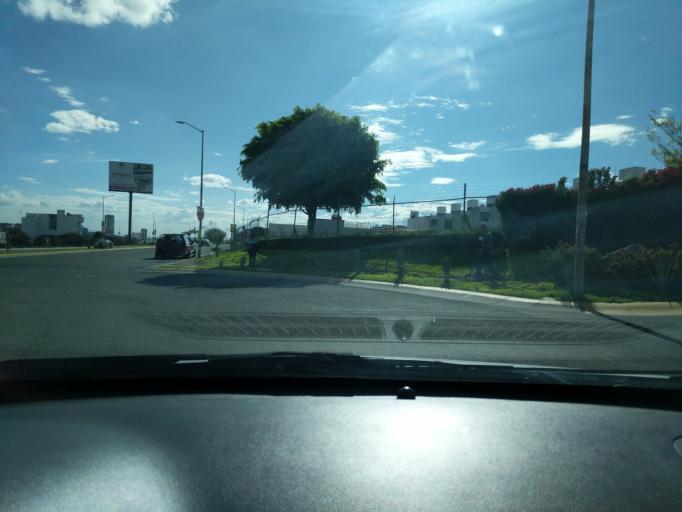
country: MX
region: Queretaro
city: La Canada
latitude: 20.5924
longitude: -100.3259
